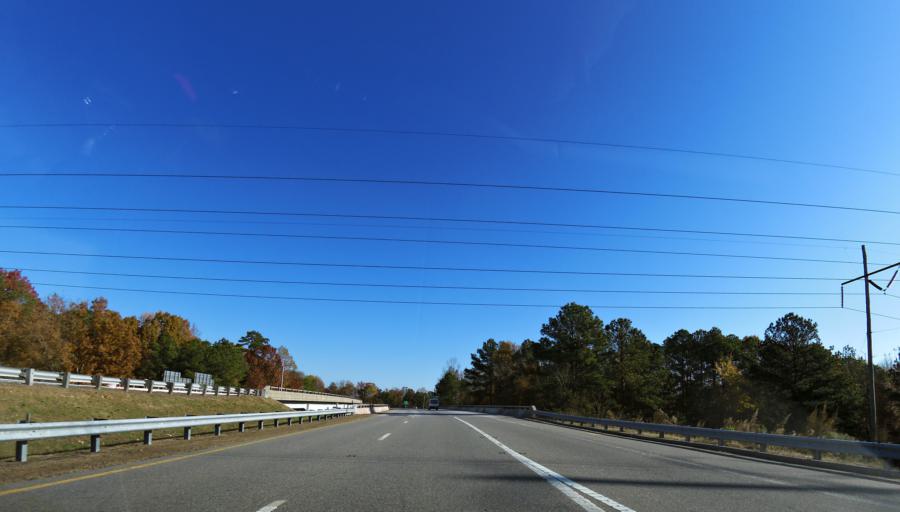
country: US
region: Virginia
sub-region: City of Williamsburg
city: Williamsburg
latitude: 37.2564
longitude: -76.6465
